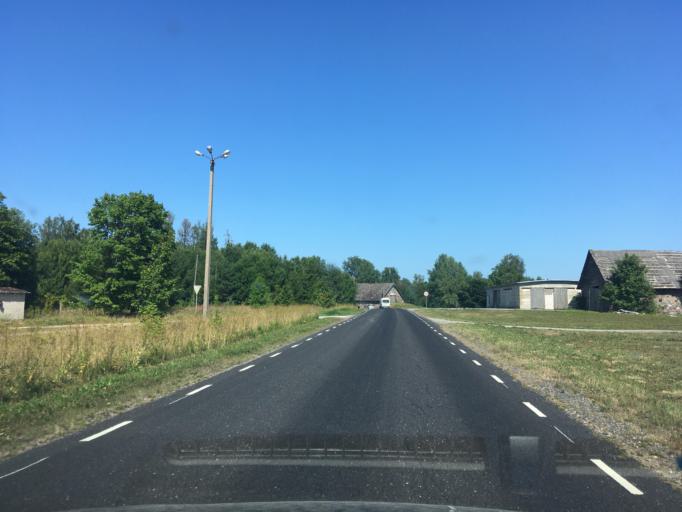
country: EE
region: Harju
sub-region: Anija vald
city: Kehra
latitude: 59.1782
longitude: 25.2228
